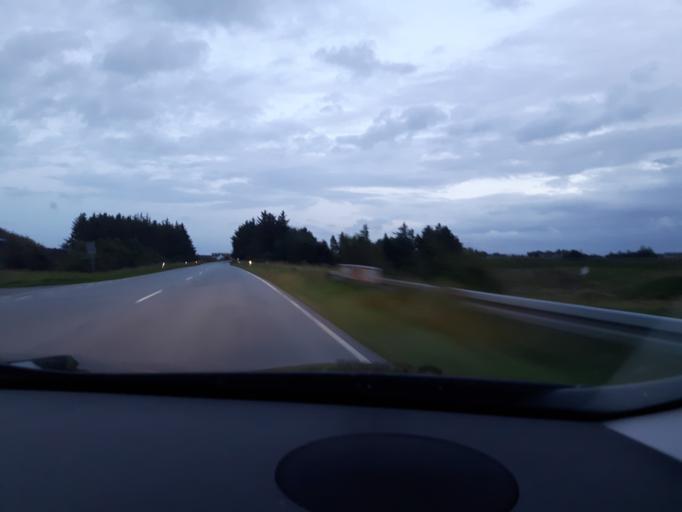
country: DK
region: North Denmark
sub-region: Hjorring Kommune
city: Hjorring
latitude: 57.4963
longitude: 9.9427
